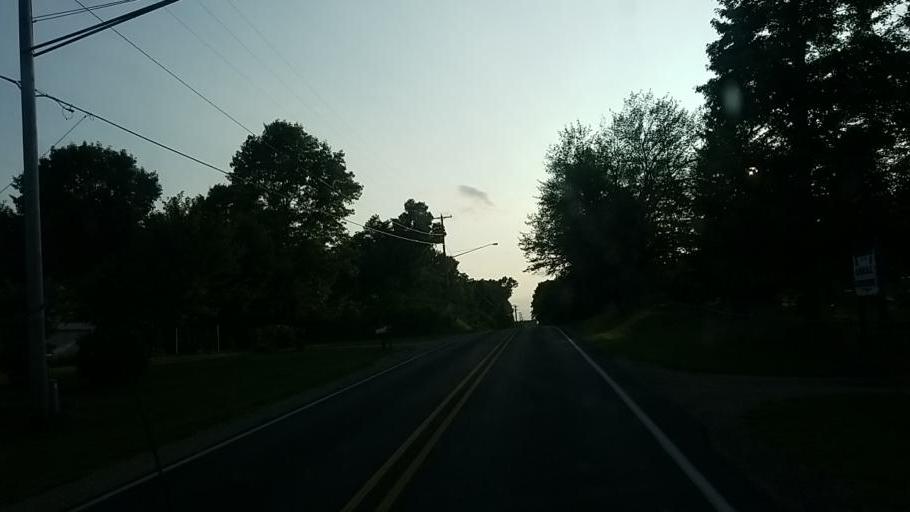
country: US
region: Michigan
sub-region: Montcalm County
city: Howard City
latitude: 43.3666
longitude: -85.4063
